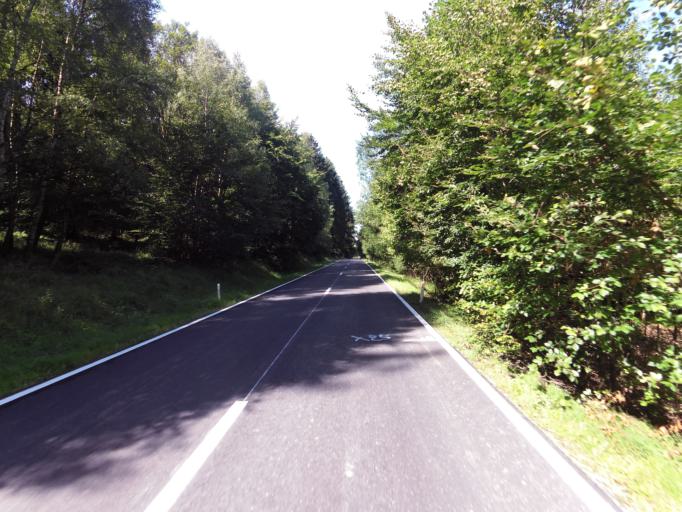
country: BE
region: Wallonia
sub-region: Province du Luxembourg
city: Nassogne
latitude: 50.1274
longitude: 5.3734
